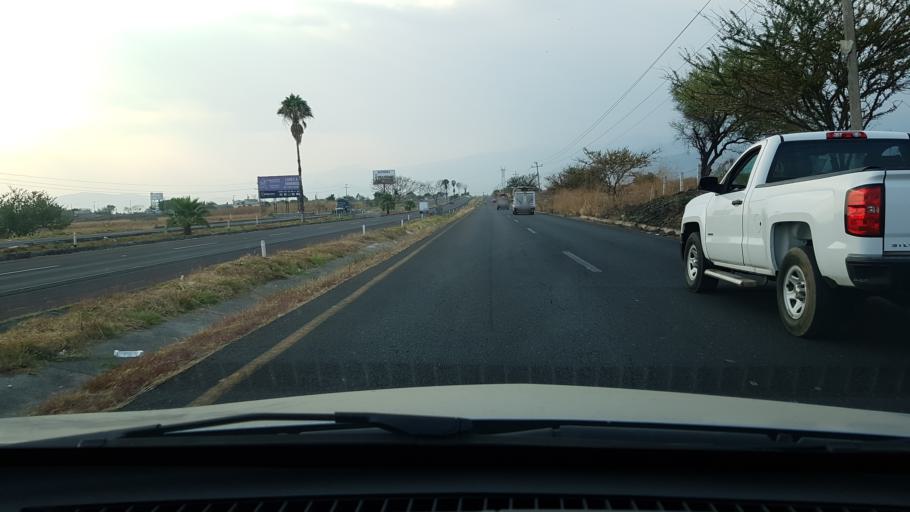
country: MX
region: Morelos
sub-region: Cuautla
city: Tierra Larga (Campo Nuevo)
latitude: 18.8710
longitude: -98.9549
